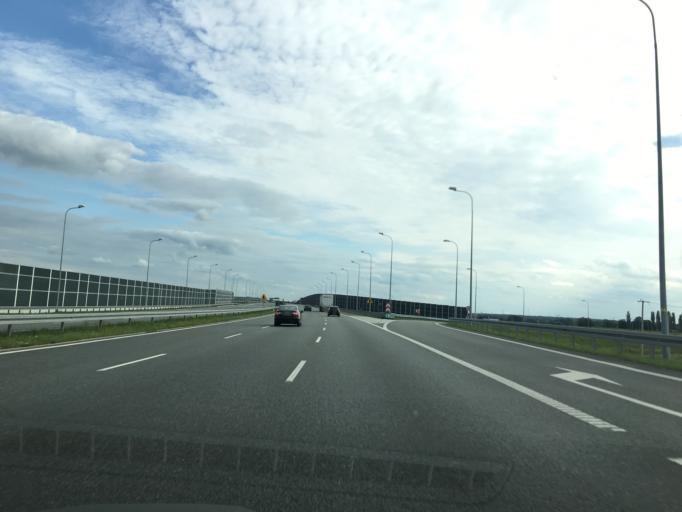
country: PL
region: Silesian Voivodeship
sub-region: Powiat tarnogorski
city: Wieszowa
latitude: 50.3495
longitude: 18.7238
